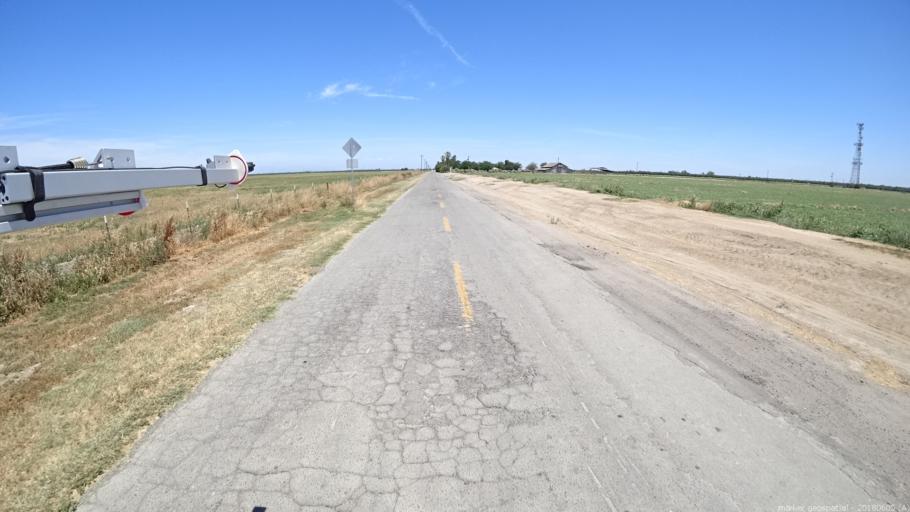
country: US
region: California
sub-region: Madera County
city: Chowchilla
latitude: 37.0907
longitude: -120.3246
